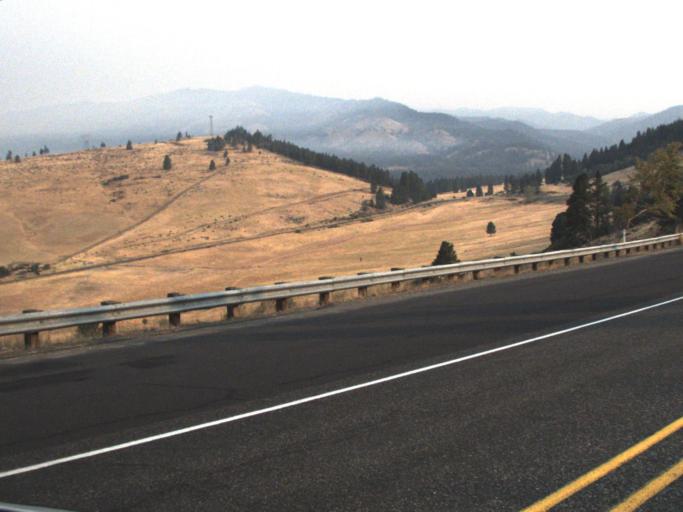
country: US
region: Washington
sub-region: Kittitas County
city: Ellensburg
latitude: 47.1681
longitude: -120.7038
